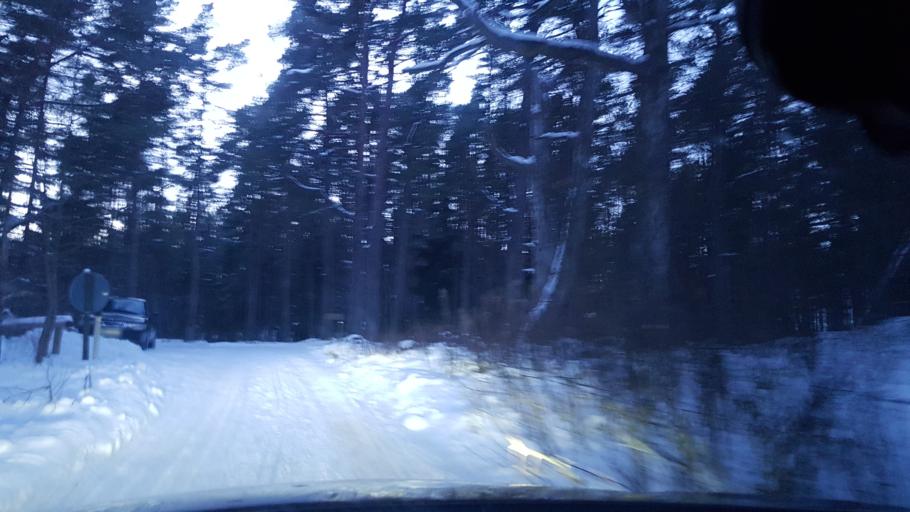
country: EE
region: Laeaene
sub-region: Haapsalu linn
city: Haapsalu
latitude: 59.2114
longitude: 23.5771
